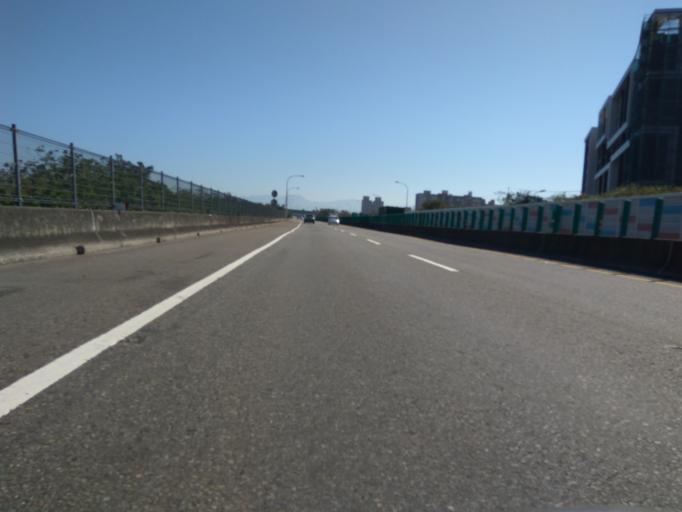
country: TW
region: Taiwan
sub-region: Hsinchu
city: Hsinchu
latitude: 24.8279
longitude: 120.9654
